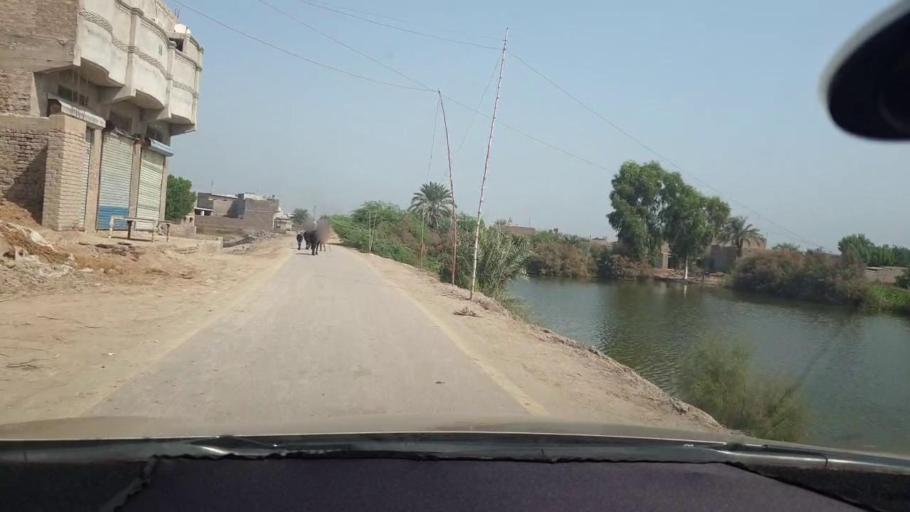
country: PK
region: Sindh
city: Kambar
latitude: 27.5797
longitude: 68.0066
